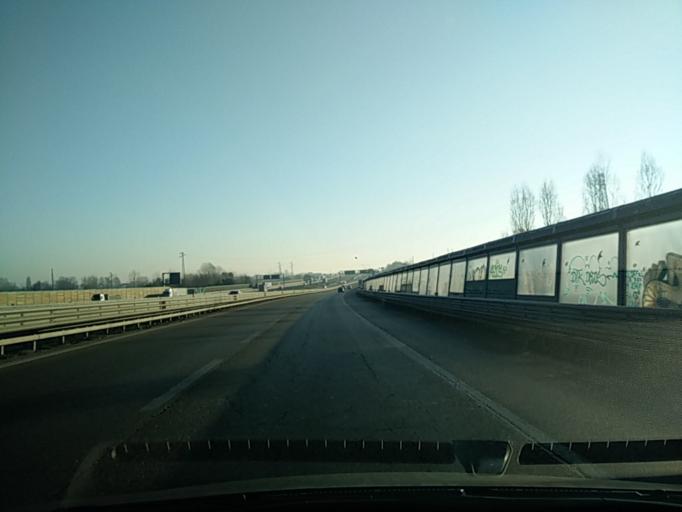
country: IT
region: Veneto
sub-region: Provincia di Padova
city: Vigodarzere
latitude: 45.4430
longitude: 11.8734
